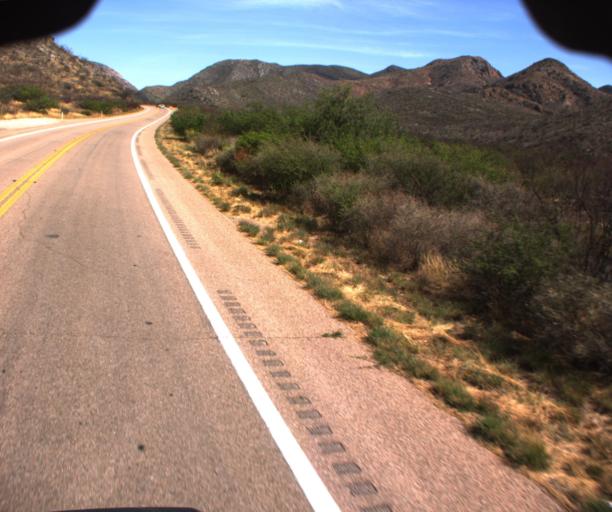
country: US
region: Arizona
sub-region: Cochise County
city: Bisbee
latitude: 31.5200
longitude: -110.0310
